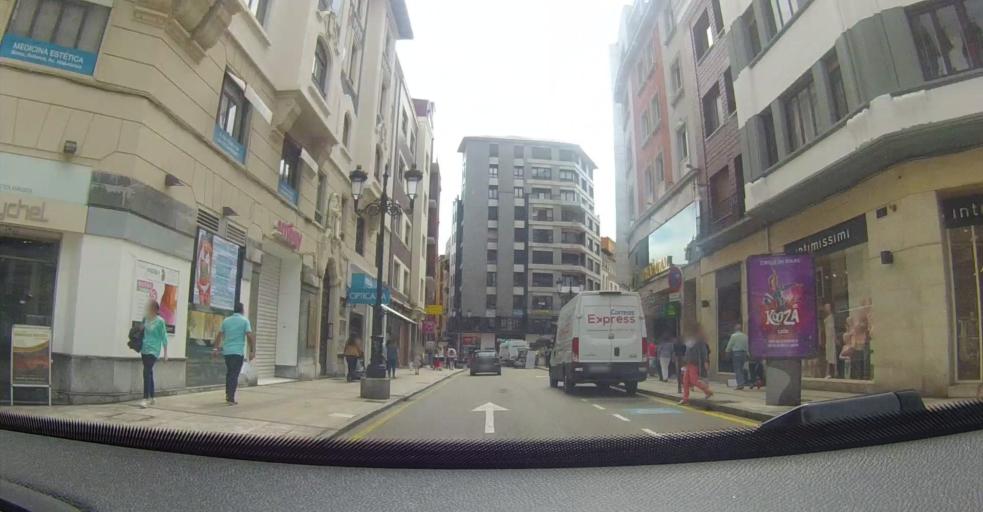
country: ES
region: Asturias
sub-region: Province of Asturias
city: Oviedo
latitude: 43.3647
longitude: -5.8506
